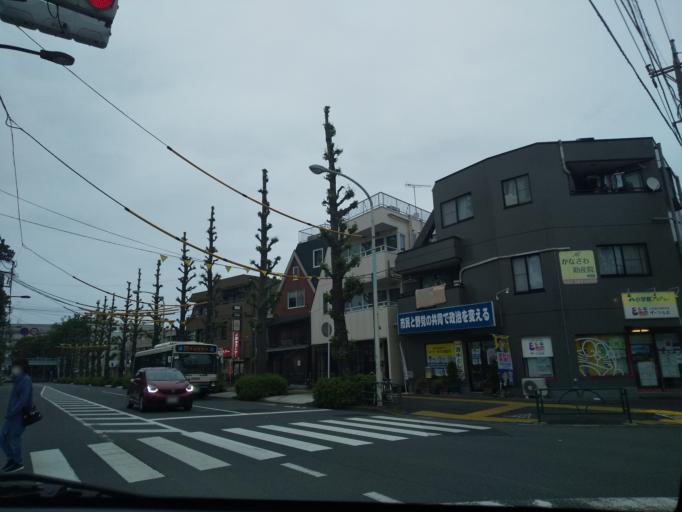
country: JP
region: Tokyo
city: Hino
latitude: 35.6639
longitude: 139.3790
